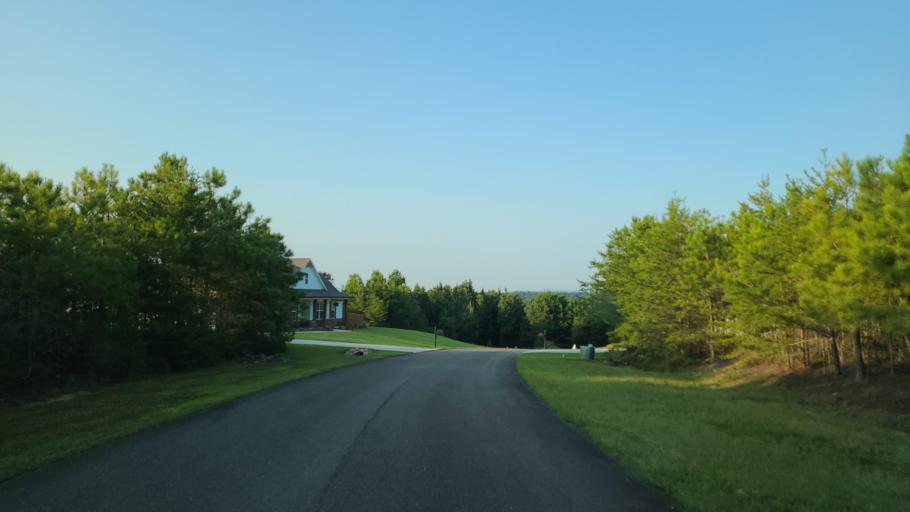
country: US
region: Georgia
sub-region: Pickens County
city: Jasper
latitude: 34.4355
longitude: -84.5466
